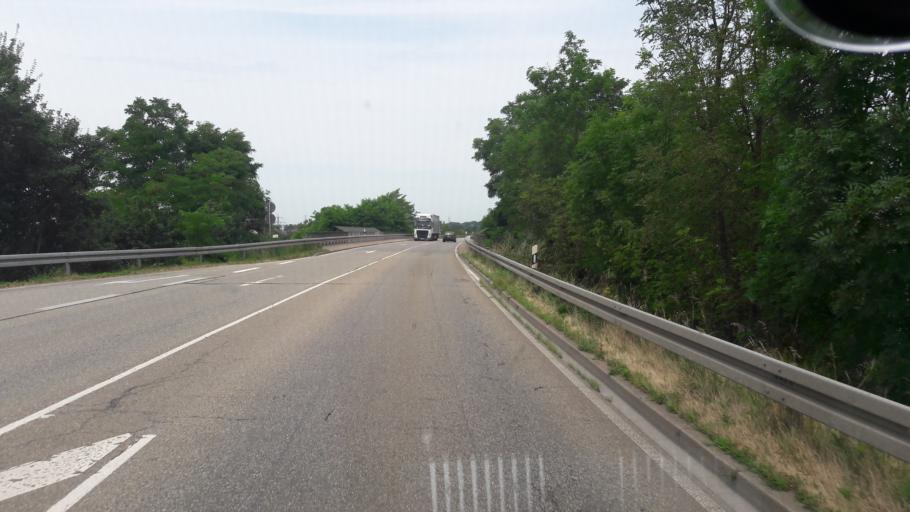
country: DE
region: Baden-Wuerttemberg
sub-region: Freiburg Region
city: Achern
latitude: 48.6277
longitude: 8.0540
